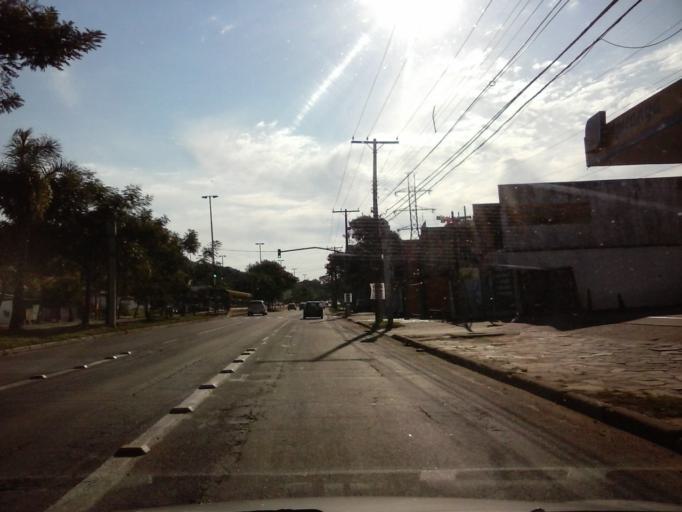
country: BR
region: Rio Grande do Sul
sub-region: Porto Alegre
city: Porto Alegre
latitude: -30.0683
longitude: -51.1458
